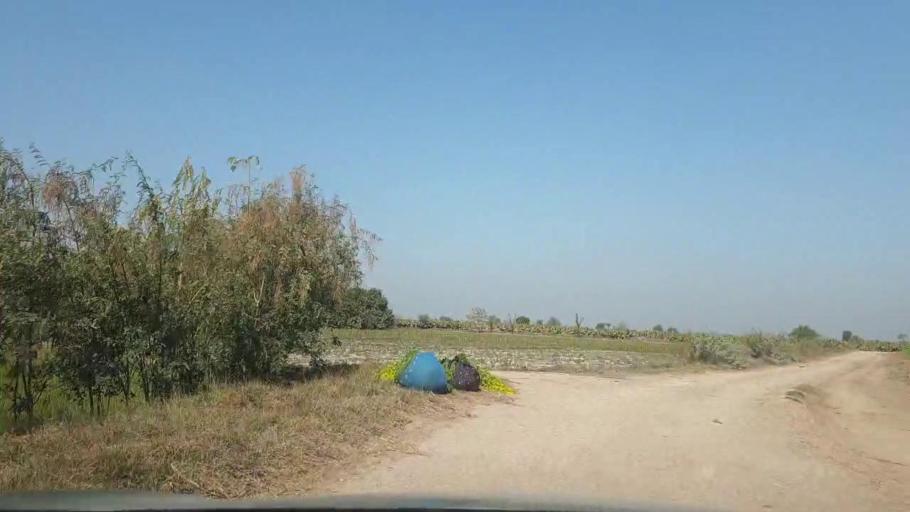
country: PK
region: Sindh
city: Tando Adam
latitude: 25.6226
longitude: 68.6439
